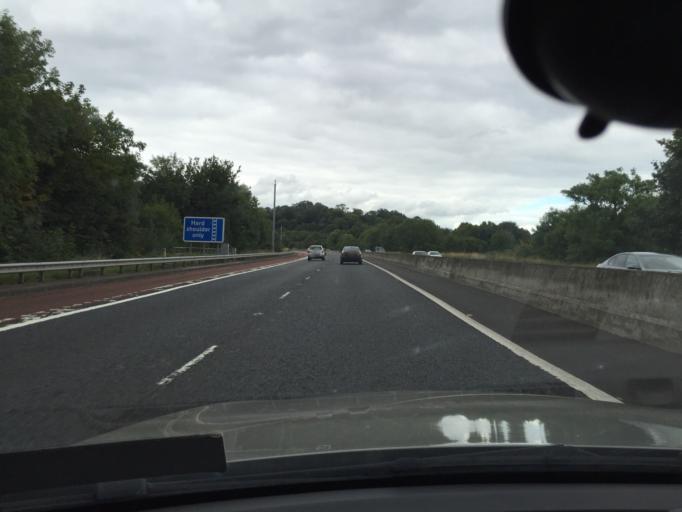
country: GB
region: Northern Ireland
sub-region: Lisburn District
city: Lisburn
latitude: 54.5383
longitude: -5.9954
